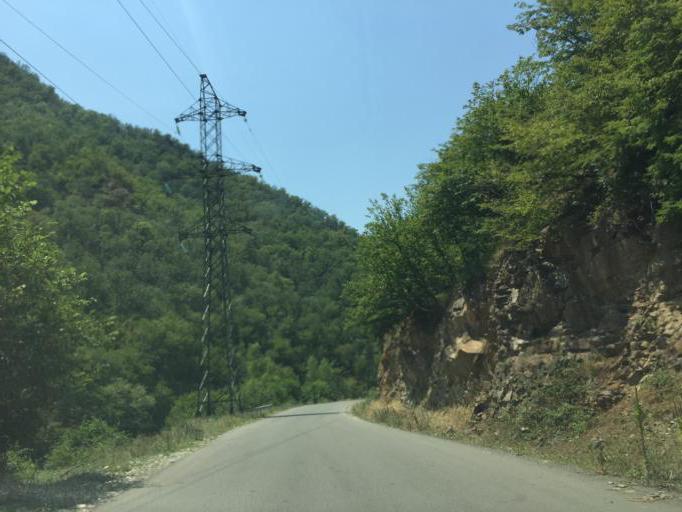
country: AZ
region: Kalbacar Rayonu
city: Kerbakhiar
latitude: 40.1346
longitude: 46.3875
